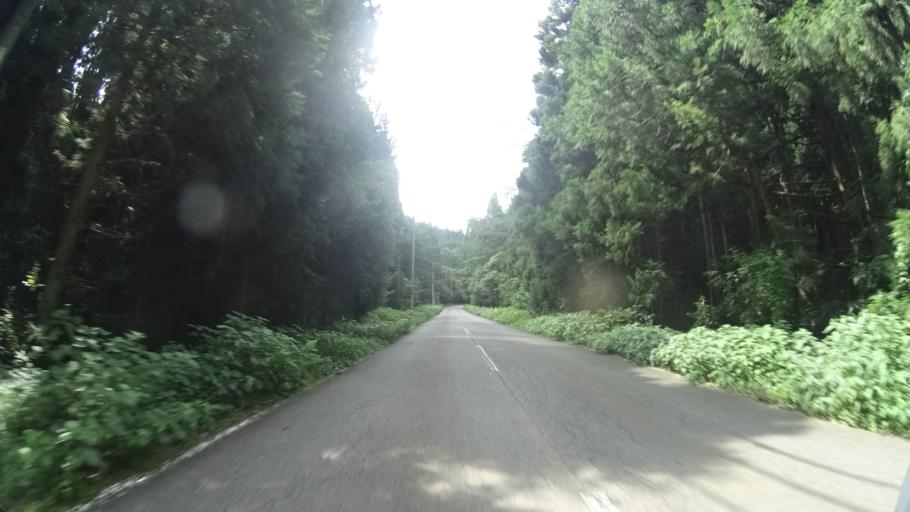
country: JP
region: Yamaguchi
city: Hagi
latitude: 34.5099
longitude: 131.5916
